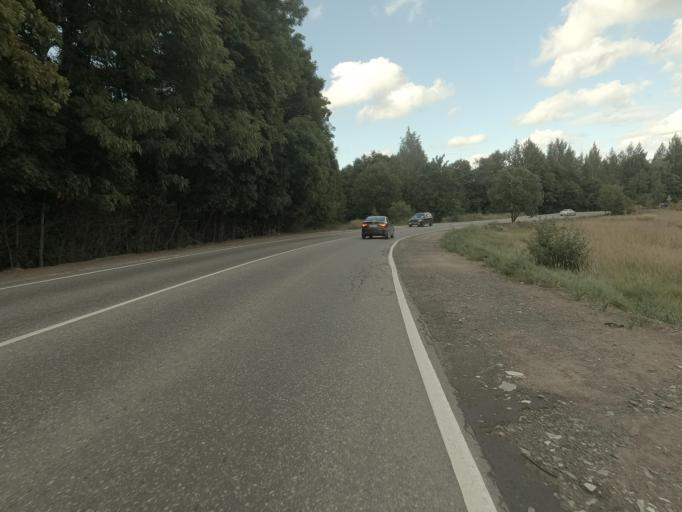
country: RU
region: Leningrad
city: Shcheglovo
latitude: 60.0287
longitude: 30.7652
